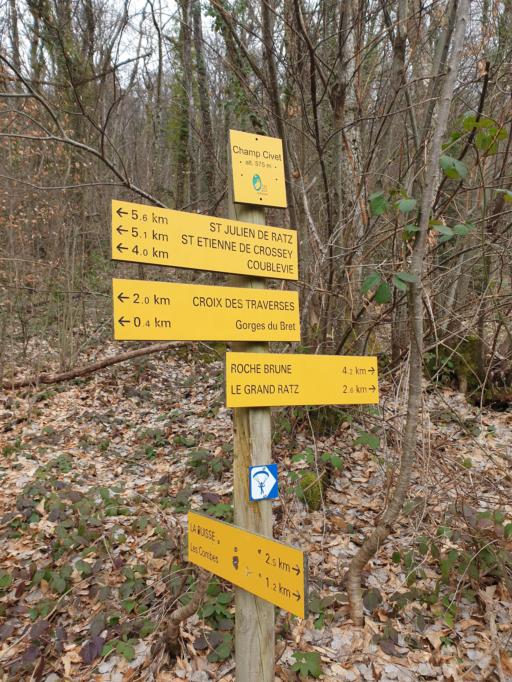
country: FR
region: Rhone-Alpes
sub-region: Departement de l'Isere
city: La Buisse
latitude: 45.3423
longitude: 5.6337
